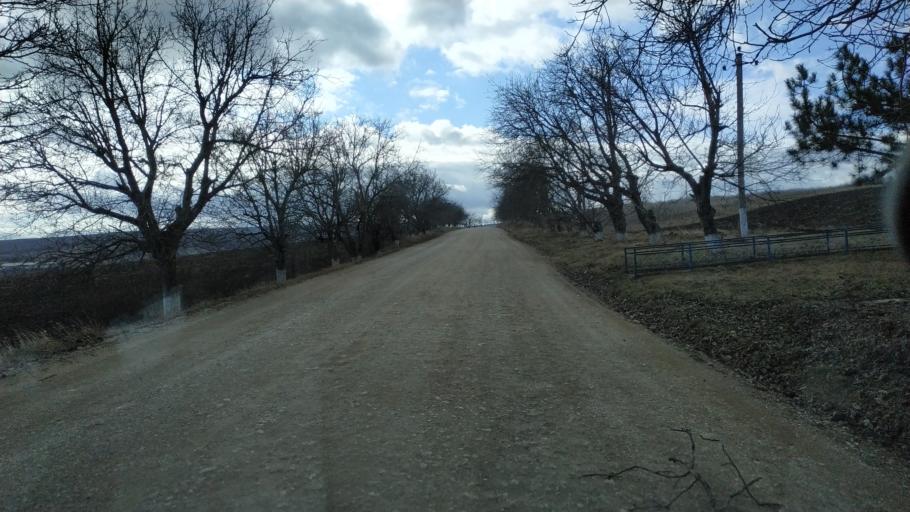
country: MD
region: Stinga Nistrului
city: Bucovat
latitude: 47.1959
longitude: 28.4888
